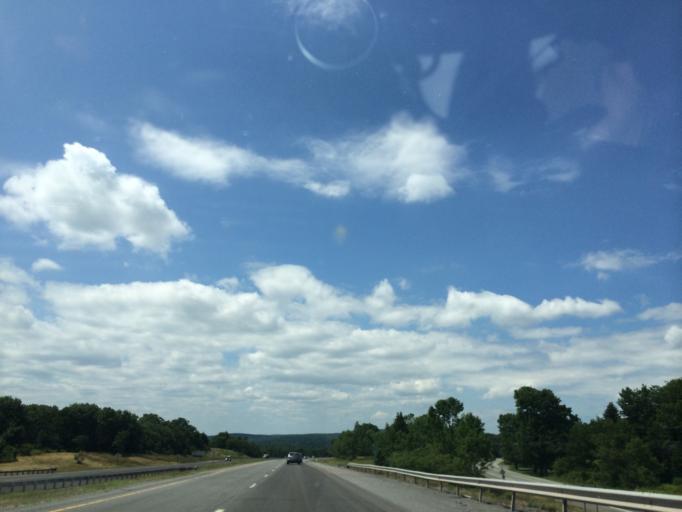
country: US
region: Pennsylvania
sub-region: Lackawanna County
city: Mount Cobb
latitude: 41.4049
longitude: -75.5199
